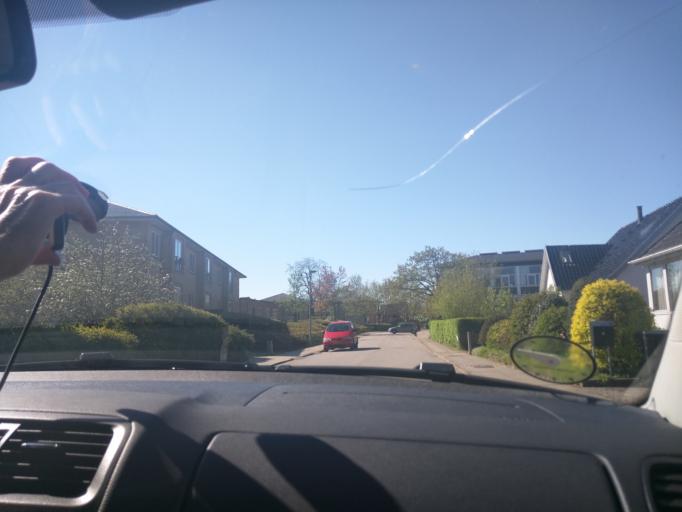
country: DK
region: Central Jutland
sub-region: Viborg Kommune
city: Viborg
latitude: 56.4483
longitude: 9.4379
